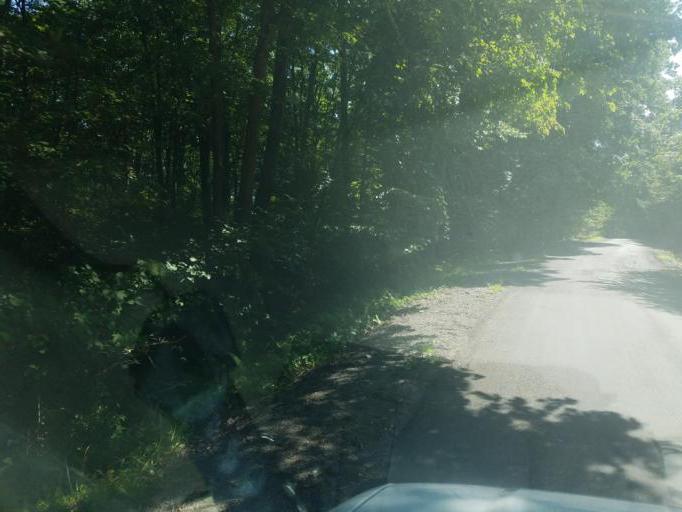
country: US
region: Pennsylvania
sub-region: Clarion County
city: Marianne
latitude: 41.1906
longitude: -79.4393
